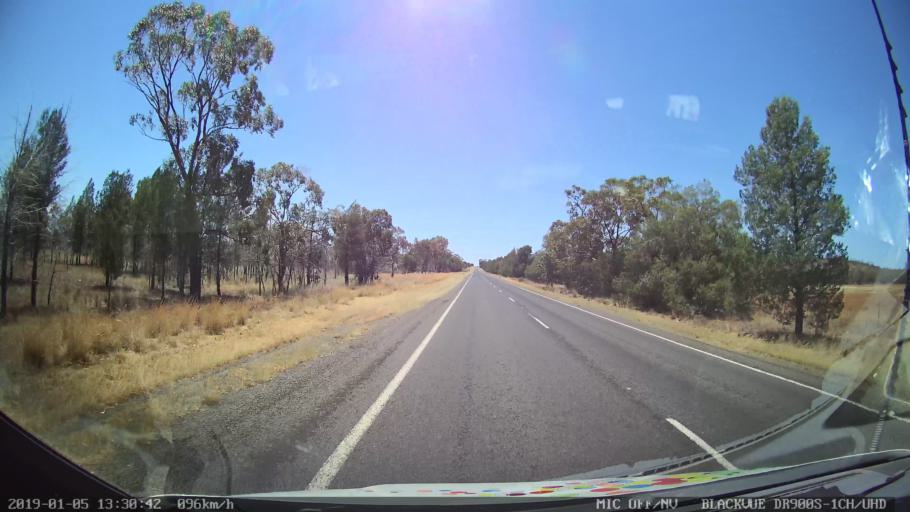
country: AU
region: New South Wales
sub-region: Gunnedah
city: Gunnedah
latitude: -31.0167
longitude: 150.0742
